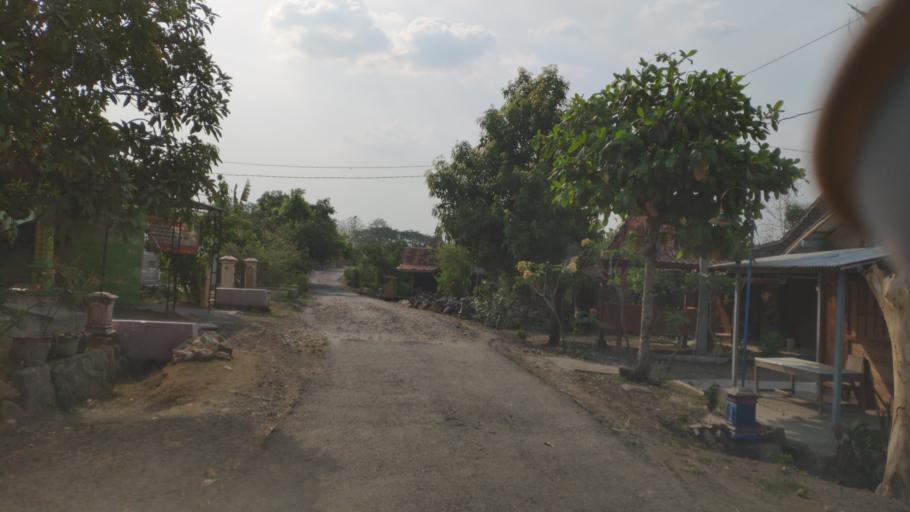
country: ID
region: Central Java
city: Randublatung
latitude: -7.2804
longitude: 111.2480
